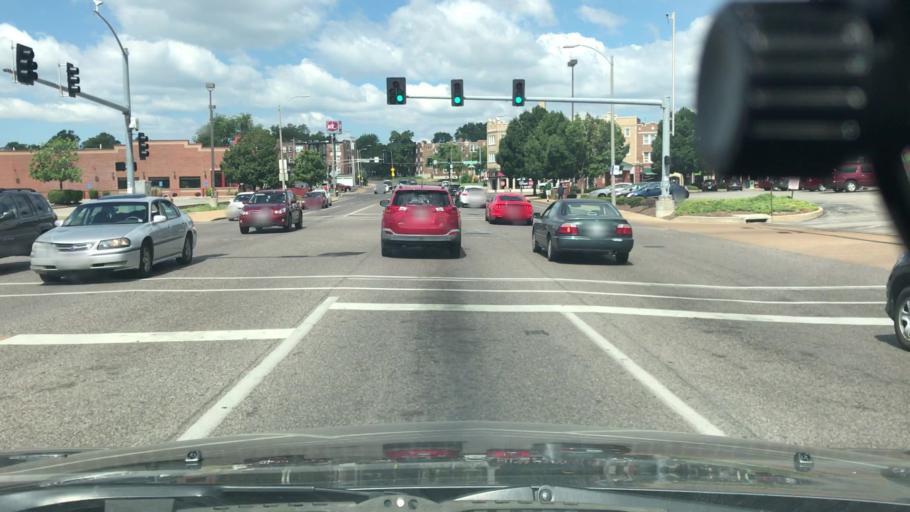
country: US
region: Missouri
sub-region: Saint Louis County
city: Maplewood
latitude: 38.5911
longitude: -90.2716
